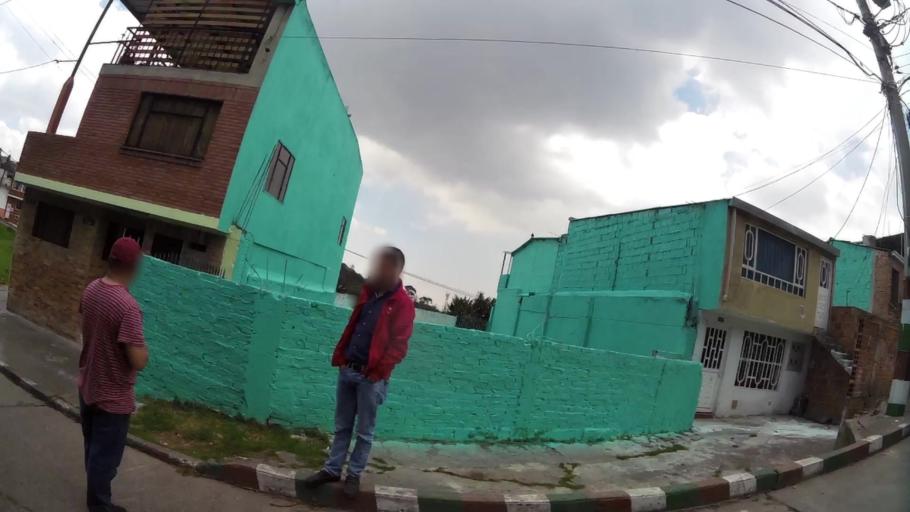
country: CO
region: Bogota D.C.
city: Bogota
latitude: 4.5861
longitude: -74.0665
